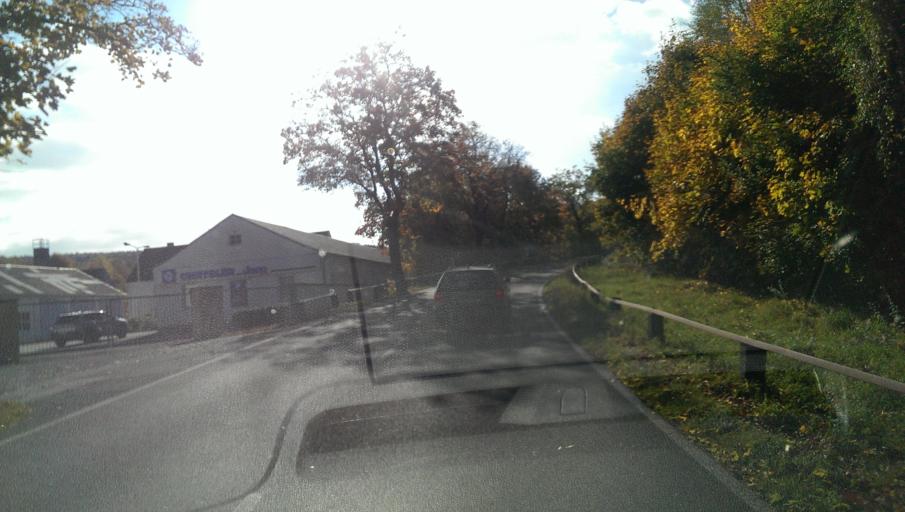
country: DE
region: Saxony
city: Dohma
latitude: 50.8723
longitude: 13.9566
